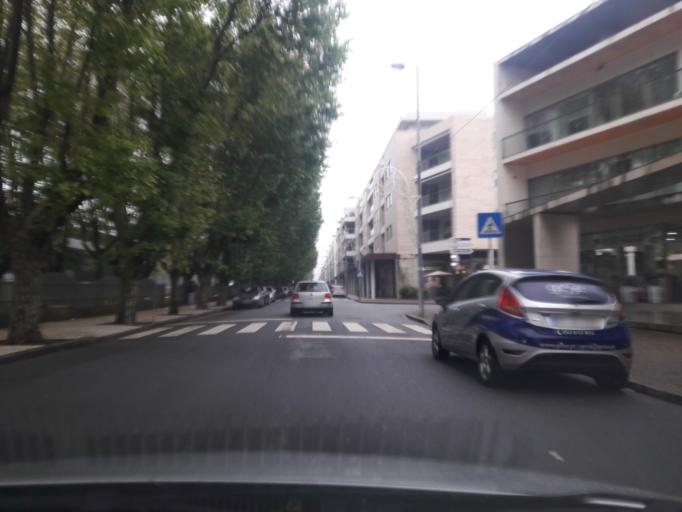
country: PT
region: Porto
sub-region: Vila do Conde
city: Vila do Conde
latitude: 41.3482
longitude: -8.7457
